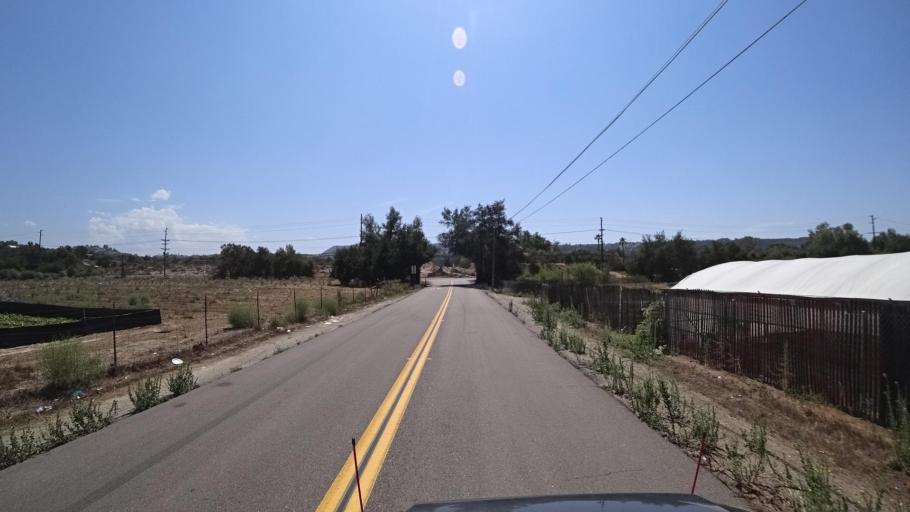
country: US
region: California
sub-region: San Diego County
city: Valley Center
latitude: 33.2293
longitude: -116.9936
